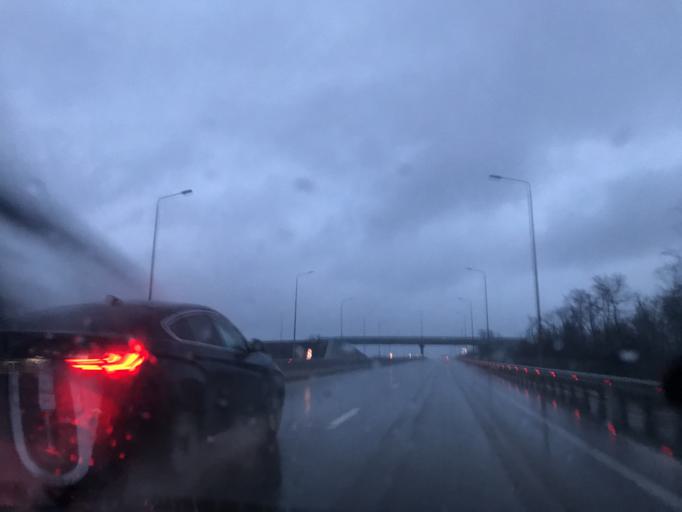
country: RU
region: Rostov
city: Samarskoye
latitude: 46.9654
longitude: 39.7189
